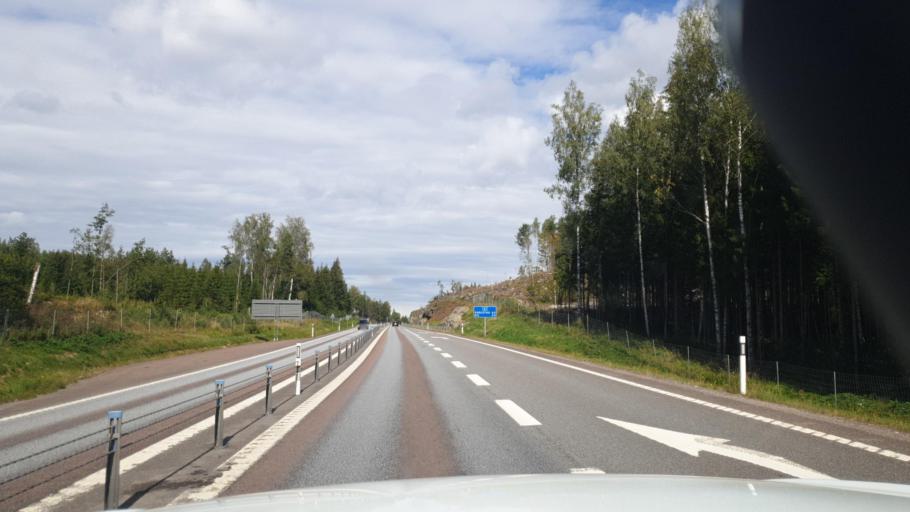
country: SE
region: Vaermland
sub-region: Arvika Kommun
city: Arvika
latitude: 59.6493
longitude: 12.7509
